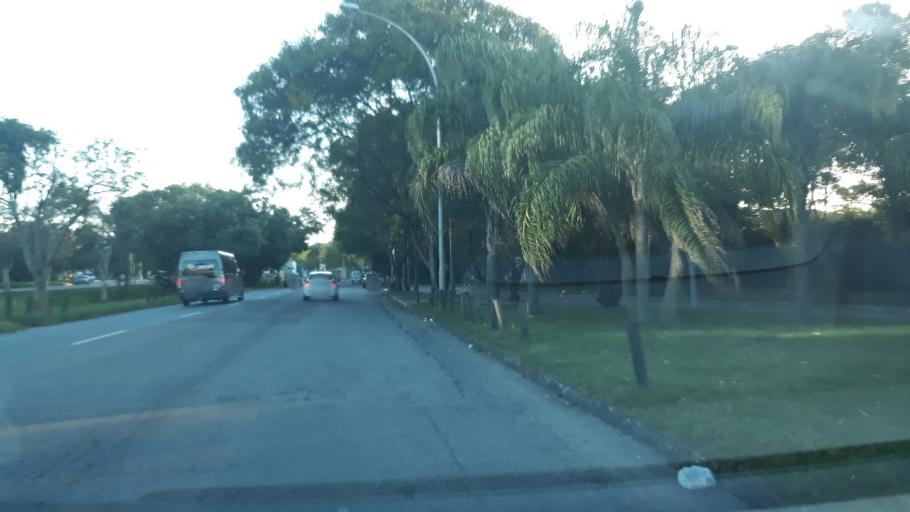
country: BR
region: Rio de Janeiro
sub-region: Rio De Janeiro
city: Rio de Janeiro
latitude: -22.9869
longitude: -43.3605
